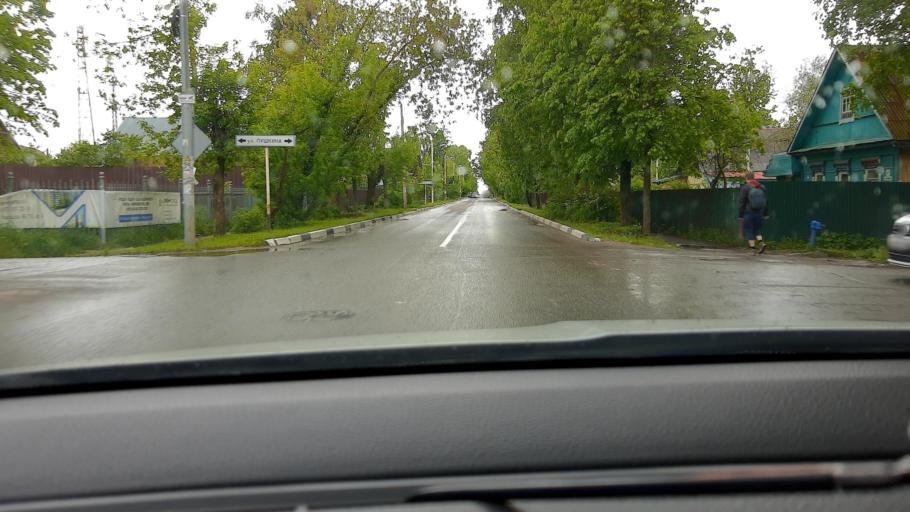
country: RU
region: Moskovskaya
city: Zvenigorod
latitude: 55.7383
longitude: 36.8623
